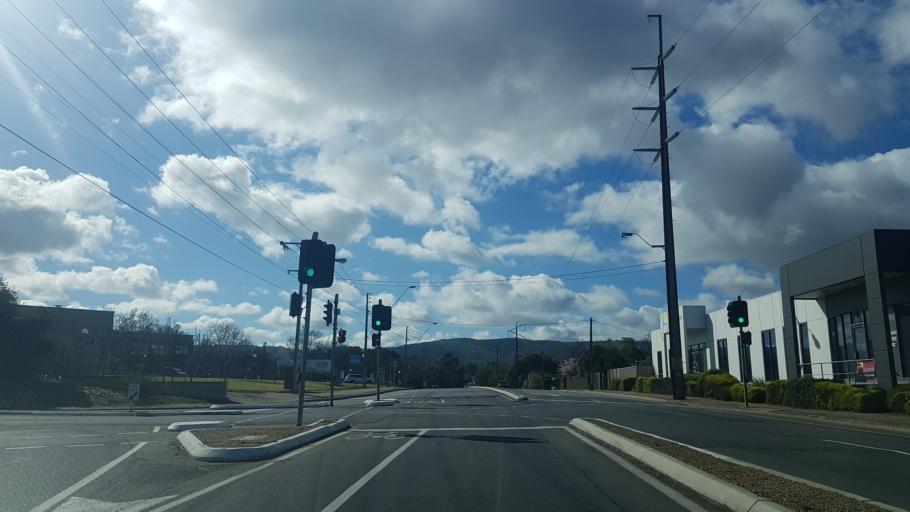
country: AU
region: South Australia
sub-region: Tea Tree Gully
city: Hope Valley
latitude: -34.8331
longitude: 138.6946
